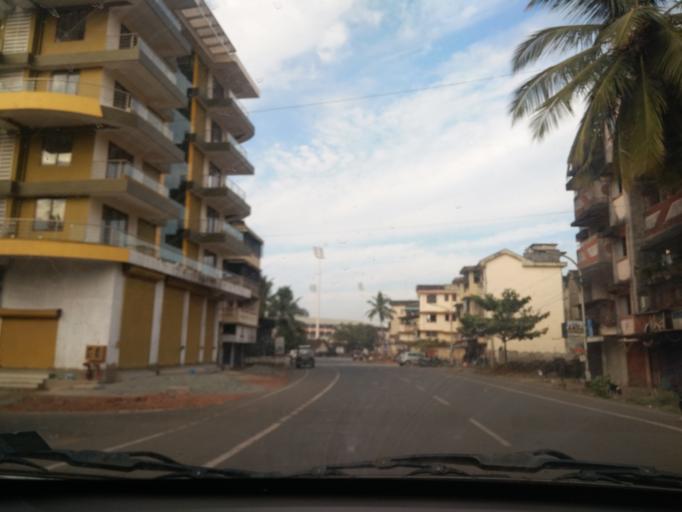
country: IN
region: Goa
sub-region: South Goa
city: Raia
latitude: 15.2904
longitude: 73.9658
